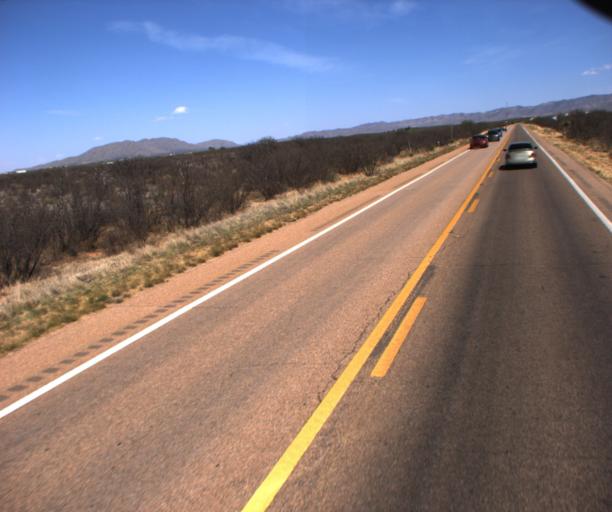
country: US
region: Arizona
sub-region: Cochise County
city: Sierra Vista Southeast
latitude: 31.5535
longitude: -110.1276
